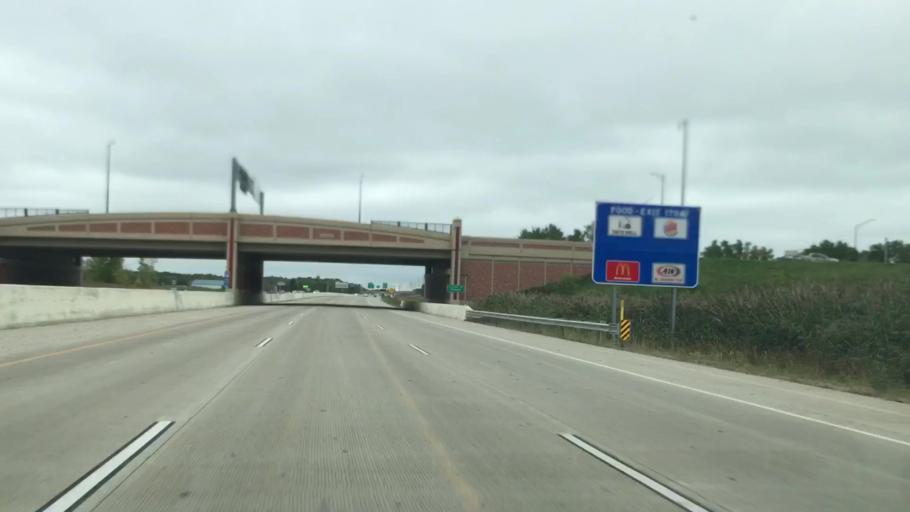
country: US
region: Wisconsin
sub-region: Brown County
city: Suamico
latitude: 44.5923
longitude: -88.0489
